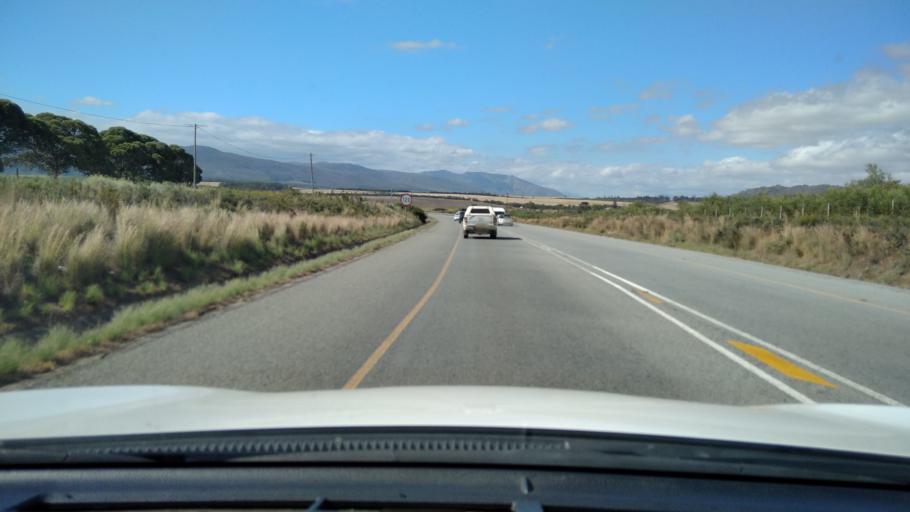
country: ZA
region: Western Cape
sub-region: Overberg District Municipality
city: Hermanus
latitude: -34.3646
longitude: 19.1425
